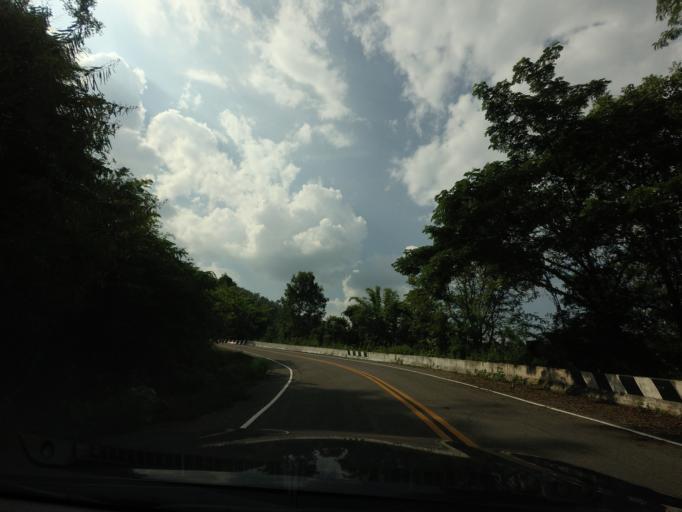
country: TH
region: Nan
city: Na Noi
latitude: 18.2860
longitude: 100.9308
